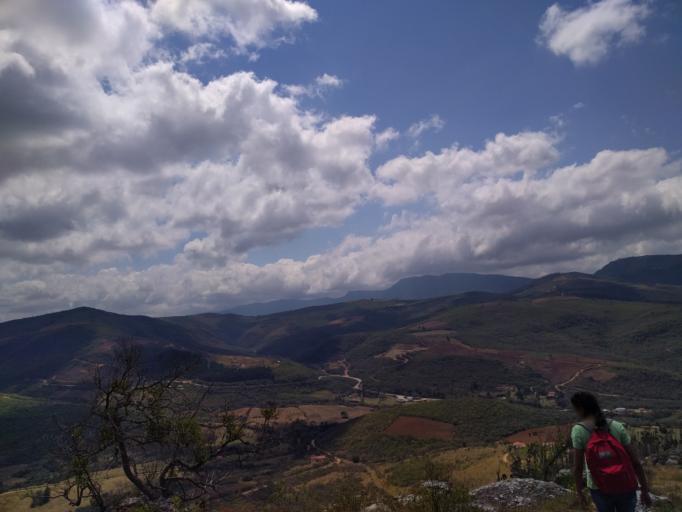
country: BO
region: Santa Cruz
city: Samaipata
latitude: -18.1801
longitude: -63.8913
